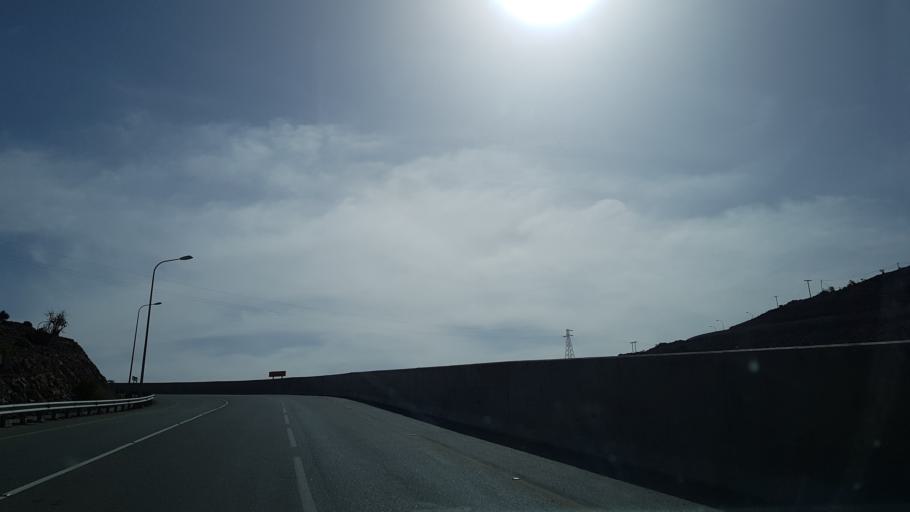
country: OM
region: Muhafazat ad Dakhiliyah
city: Izki
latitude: 23.0725
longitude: 57.7125
